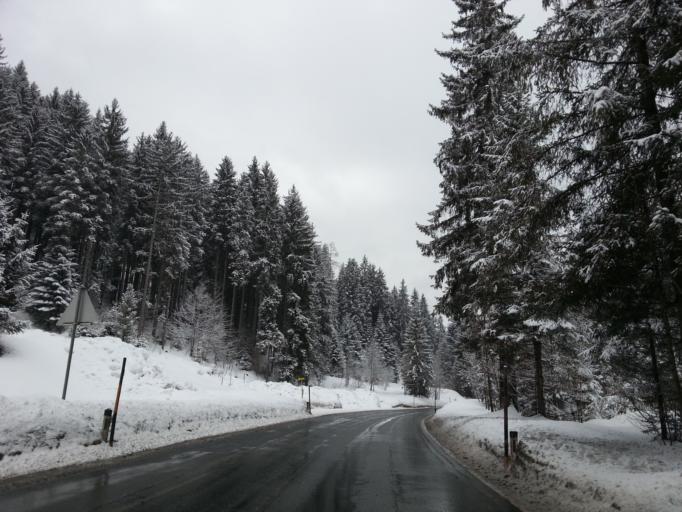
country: AT
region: Salzburg
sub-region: Politischer Bezirk Sankt Johann im Pongau
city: Eben im Pongau
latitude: 47.4886
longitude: 13.3968
